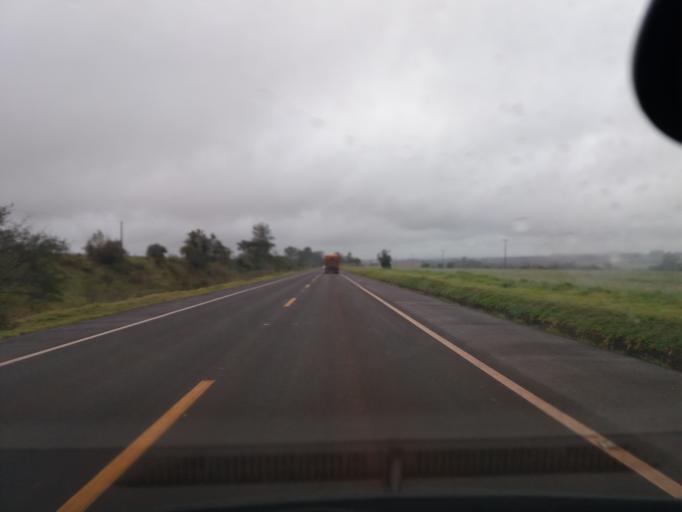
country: BR
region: Parana
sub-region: Campo Mourao
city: Campo Mourao
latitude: -24.0951
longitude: -52.4251
